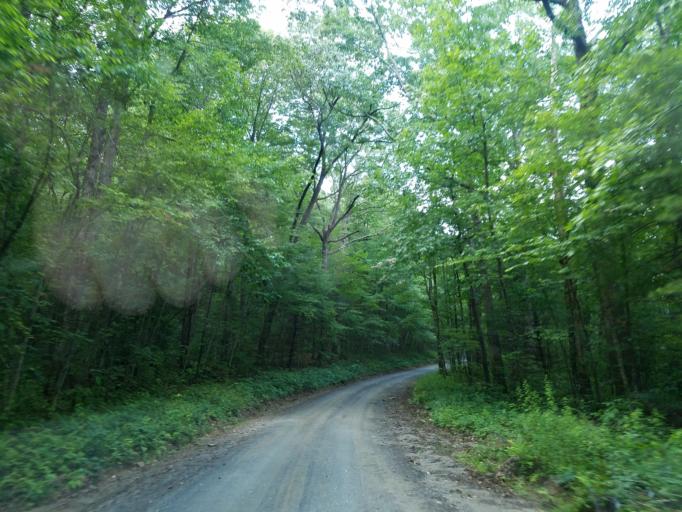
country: US
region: Georgia
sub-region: Fannin County
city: Blue Ridge
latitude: 34.6486
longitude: -84.2148
